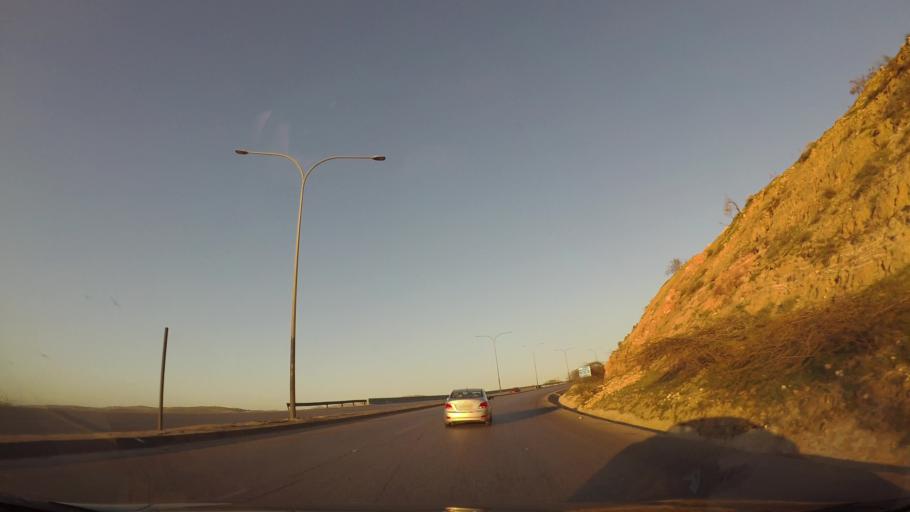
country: JO
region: Balqa
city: Yarqa
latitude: 31.8694
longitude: 35.7324
